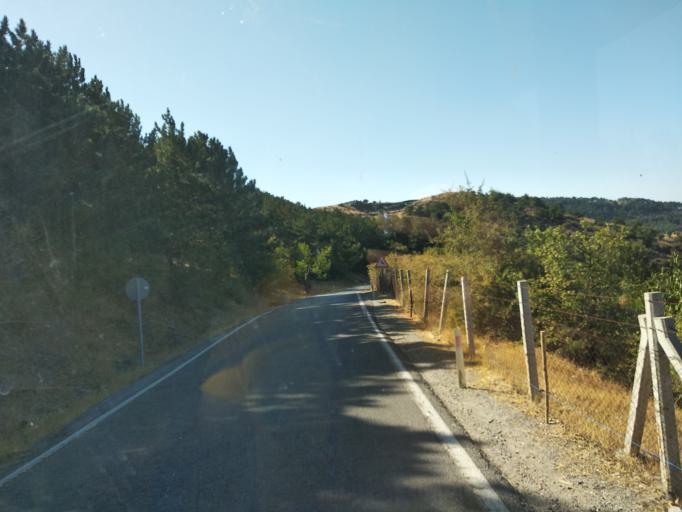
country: TR
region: Izmir
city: Gaziemir
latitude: 38.3200
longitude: 27.0093
